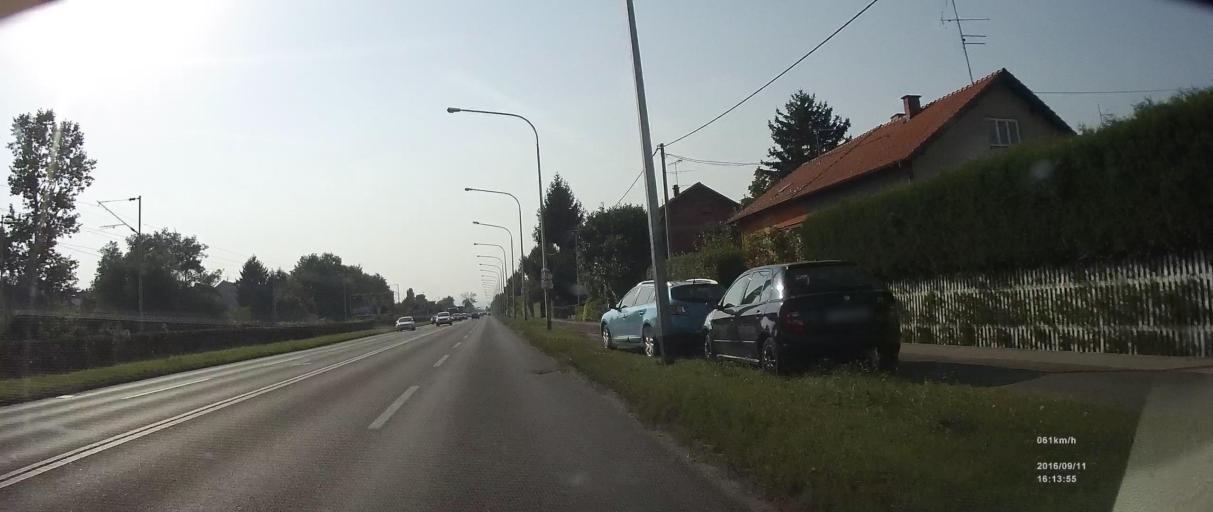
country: HR
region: Grad Zagreb
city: Stenjevec
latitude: 45.8126
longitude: 15.8944
